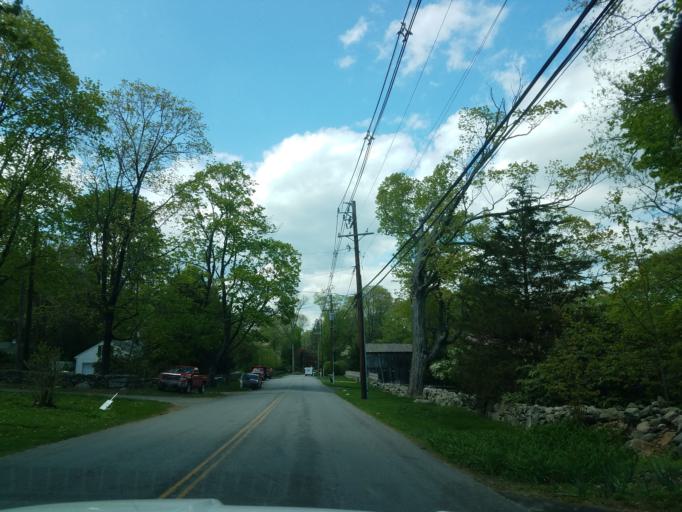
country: US
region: Connecticut
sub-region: Fairfield County
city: New Canaan
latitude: 41.1286
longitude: -73.4756
